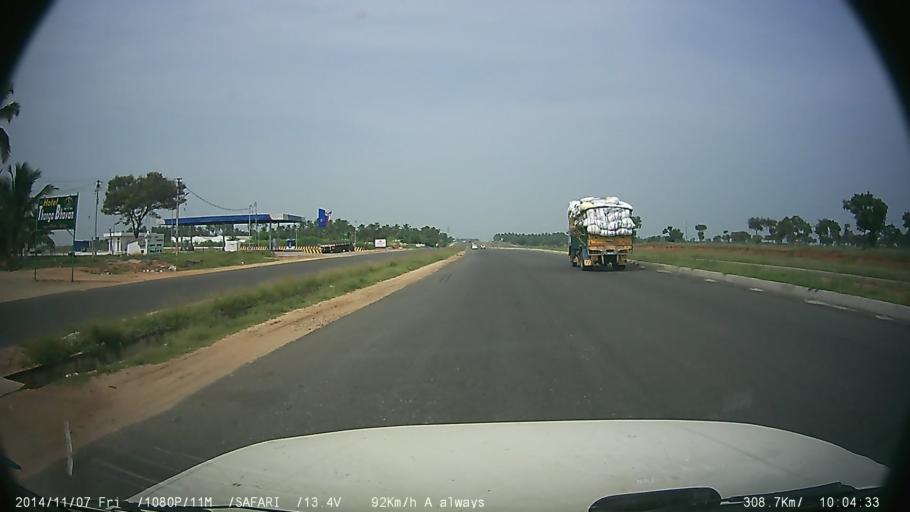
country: IN
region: Tamil Nadu
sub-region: Tiruppur
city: Uttukkuli
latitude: 11.2064
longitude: 77.3838
